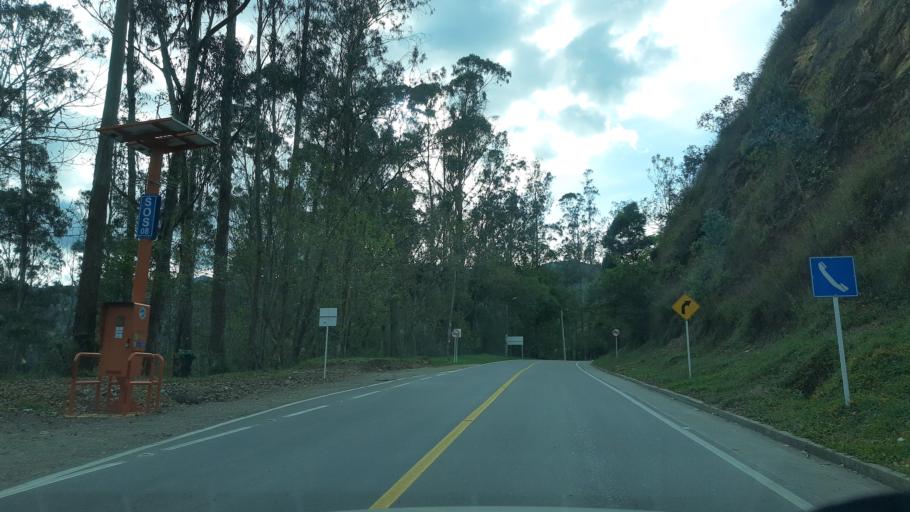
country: CO
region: Cundinamarca
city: Macheta
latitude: 5.0827
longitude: -73.6111
